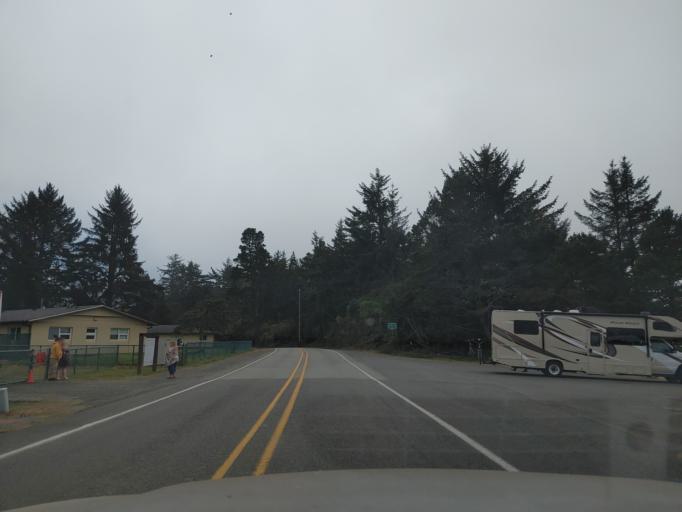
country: US
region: Oregon
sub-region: Coos County
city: Lakeside
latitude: 43.6625
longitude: -124.1988
